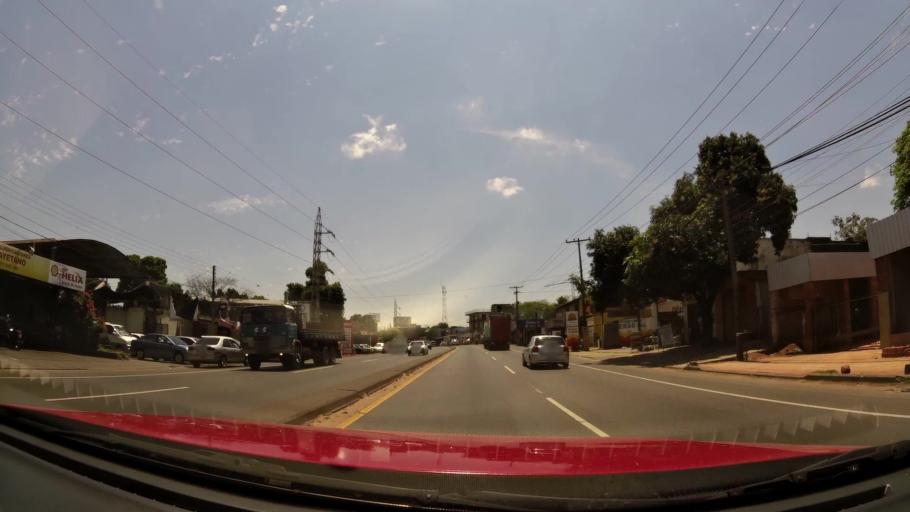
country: PY
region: Central
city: Villa Elisa
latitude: -25.3511
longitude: -57.5725
